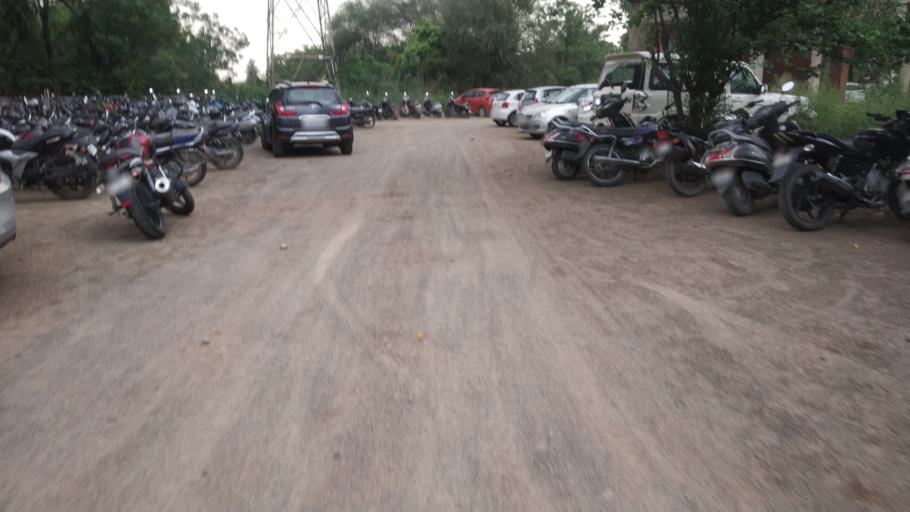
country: IN
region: Punjab
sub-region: Ajitgarh
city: Mohali
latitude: 30.7130
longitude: 76.7081
